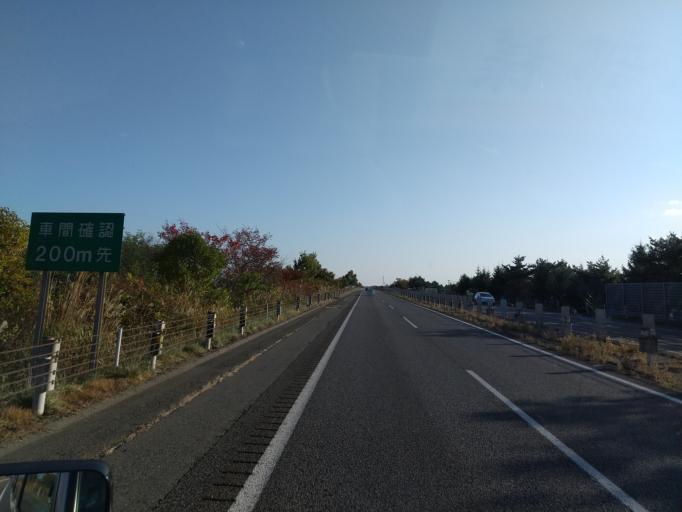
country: JP
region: Iwate
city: Morioka-shi
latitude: 39.6394
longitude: 141.1262
